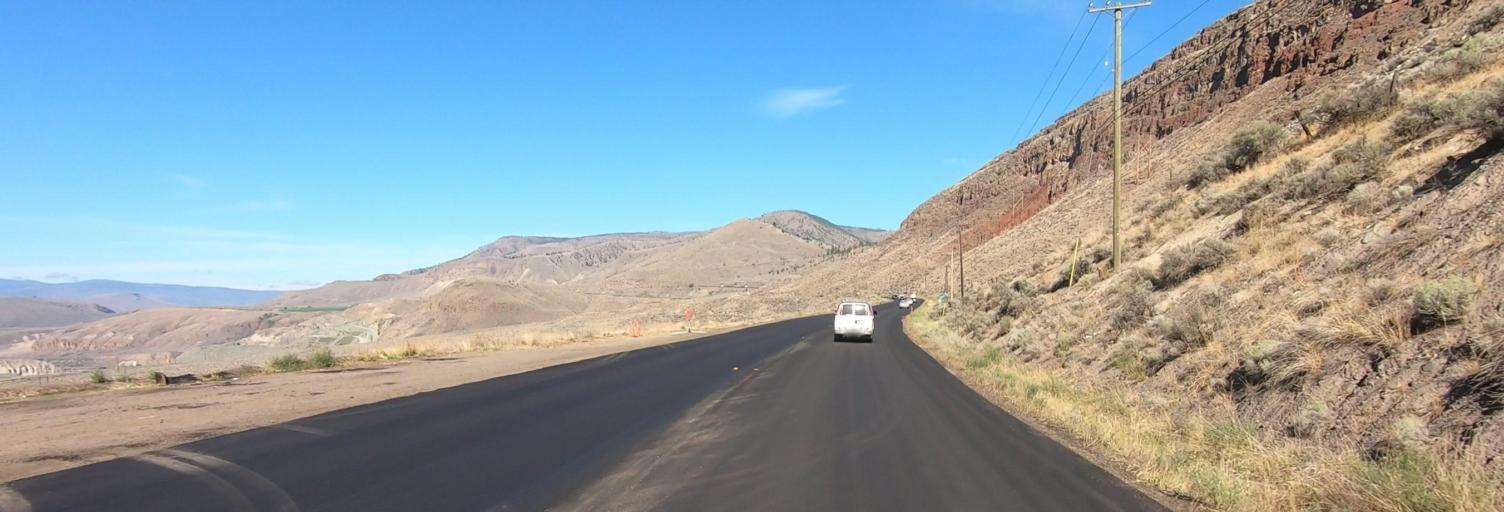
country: CA
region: British Columbia
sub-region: Thompson-Nicola Regional District
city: Ashcroft
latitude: 50.7923
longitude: -121.0870
